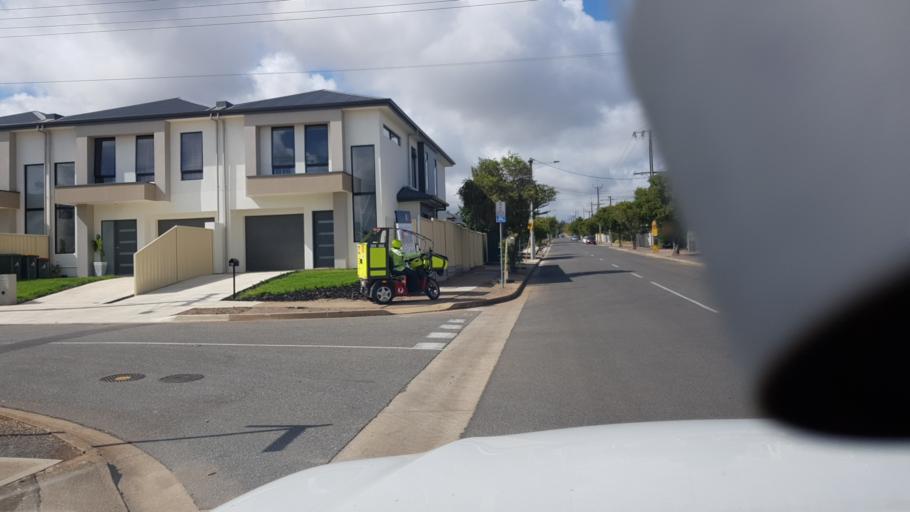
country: AU
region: South Australia
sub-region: Holdfast Bay
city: Seacliff Park
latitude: -35.0264
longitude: 138.5327
